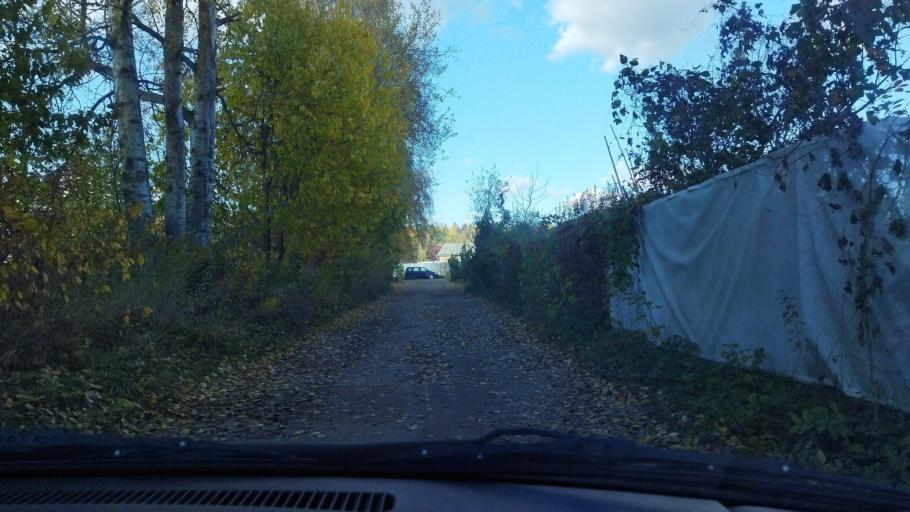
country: BY
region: Minsk
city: Slabada
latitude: 53.9876
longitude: 27.8996
